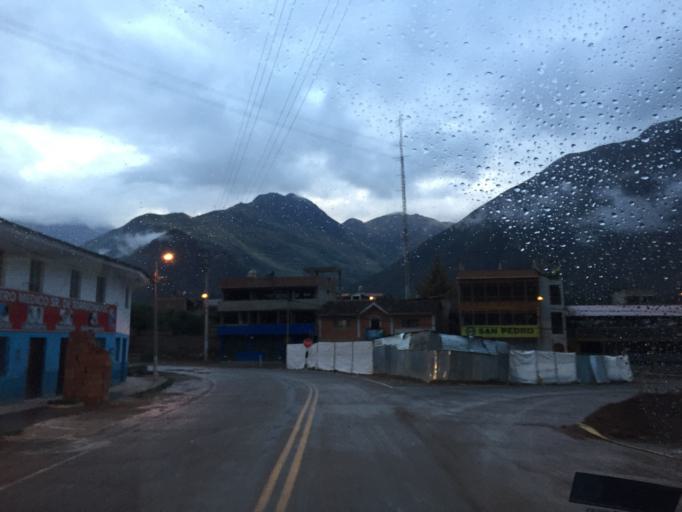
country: PE
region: Cusco
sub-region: Provincia de Urubamba
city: Urubamba
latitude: -13.3111
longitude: -72.1106
